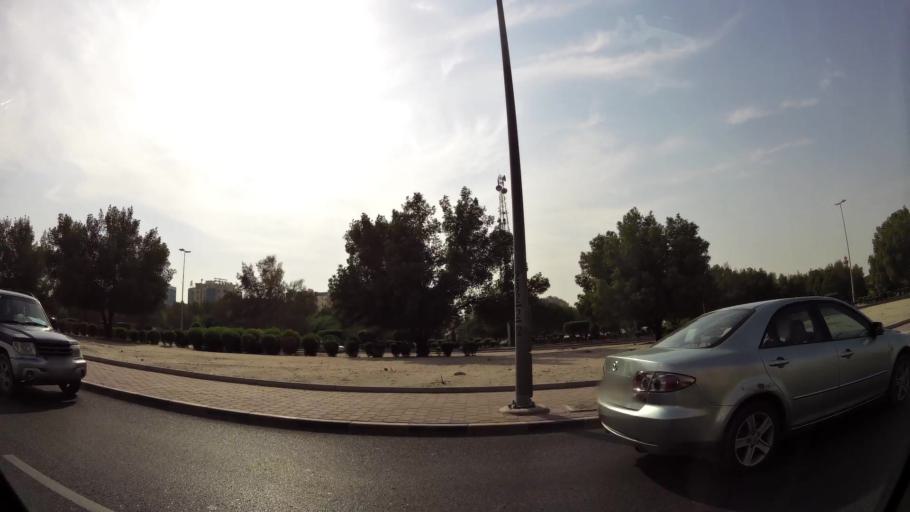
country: KW
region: Al Farwaniyah
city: Al Farwaniyah
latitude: 29.2788
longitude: 47.9687
